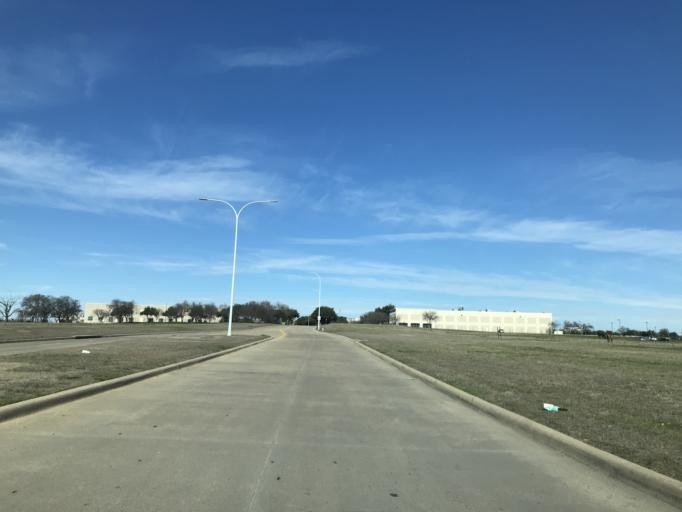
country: US
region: Texas
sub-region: Tarrant County
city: Haltom City
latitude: 32.8248
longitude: -97.2998
